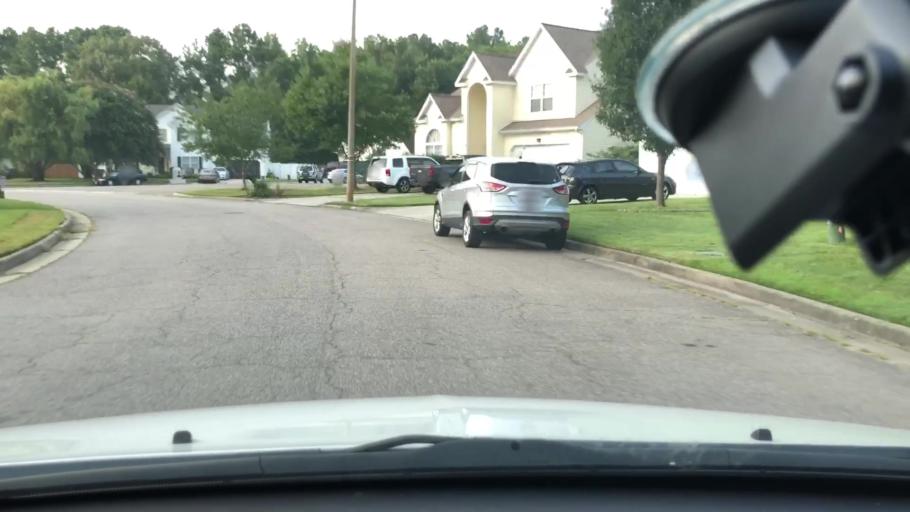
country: US
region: Virginia
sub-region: City of Chesapeake
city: Chesapeake
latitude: 36.7250
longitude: -76.2734
